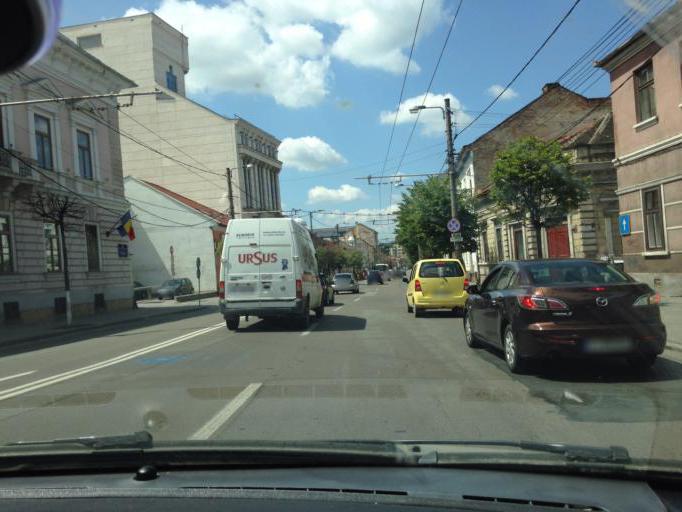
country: RO
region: Cluj
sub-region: Municipiul Cluj-Napoca
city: Cluj-Napoca
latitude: 46.7685
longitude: 23.5845
